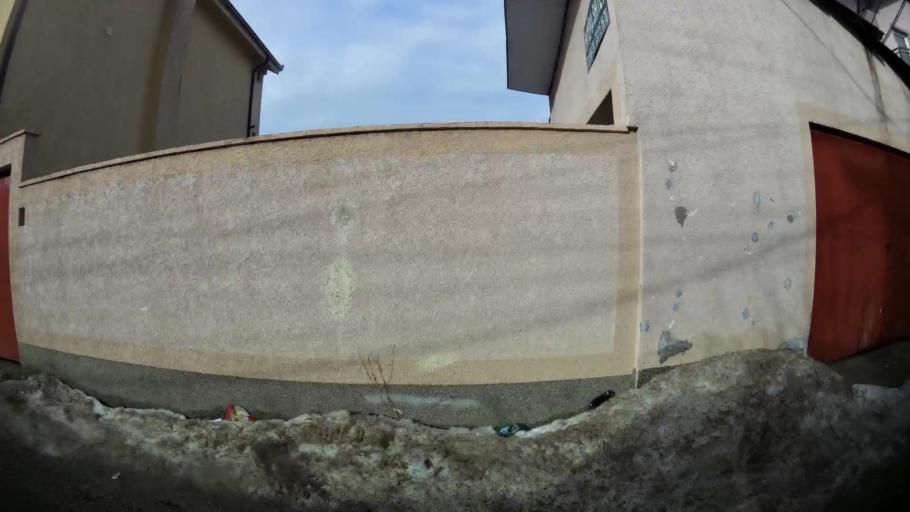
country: XK
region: Pristina
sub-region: Komuna e Prishtines
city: Pristina
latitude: 42.6706
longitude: 21.1746
